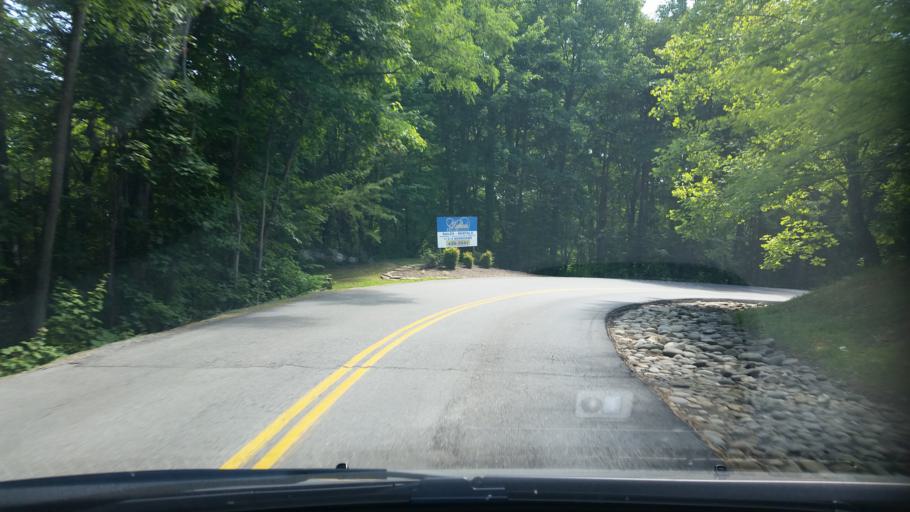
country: US
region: Tennessee
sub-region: Sevier County
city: Gatlinburg
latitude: 35.7134
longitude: -83.5305
